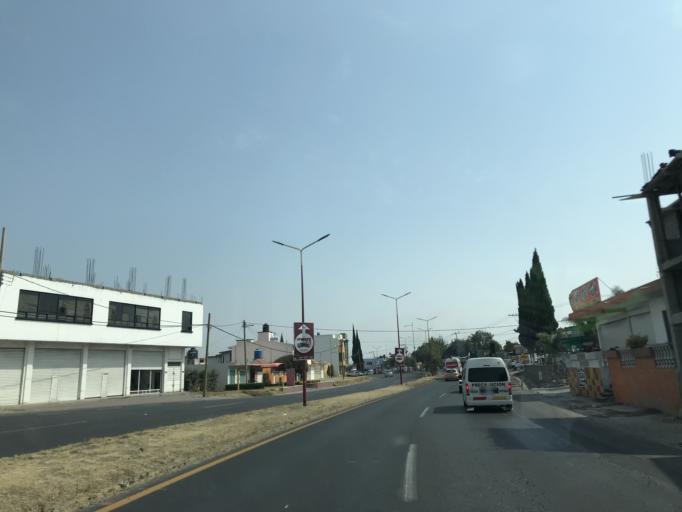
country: MX
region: Tlaxcala
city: La Magdalena Tlaltelulco
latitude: 19.2853
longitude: -98.1956
